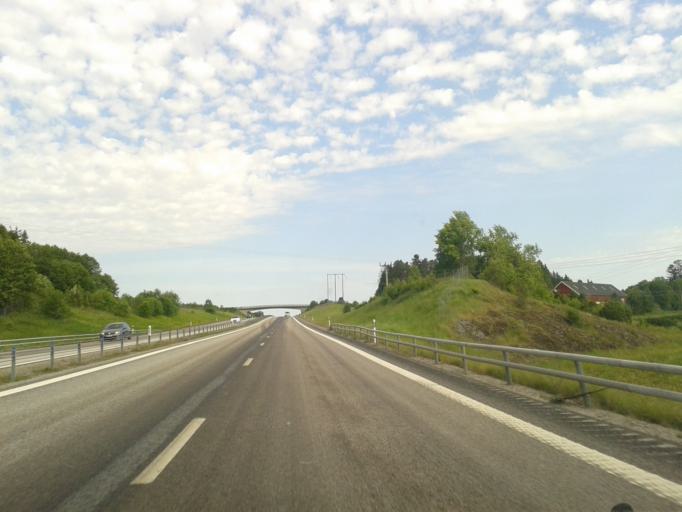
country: SE
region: Vaestra Goetaland
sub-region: Munkedals Kommun
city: Munkedal
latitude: 58.5038
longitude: 11.5642
